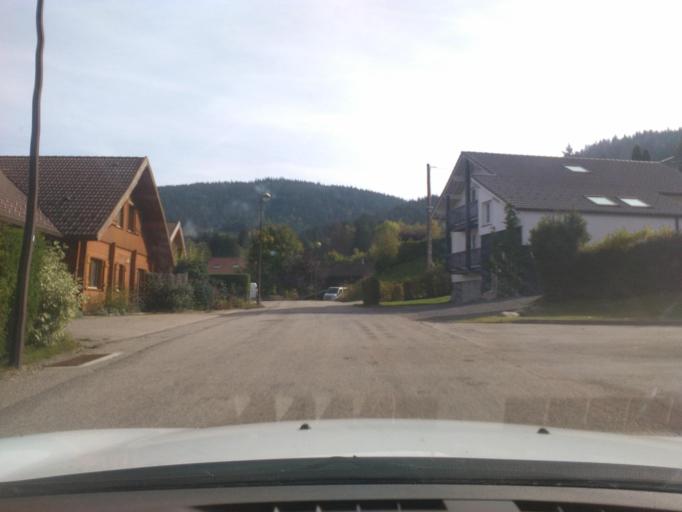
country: FR
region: Lorraine
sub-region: Departement des Vosges
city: Gerardmer
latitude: 48.0634
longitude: 6.8727
